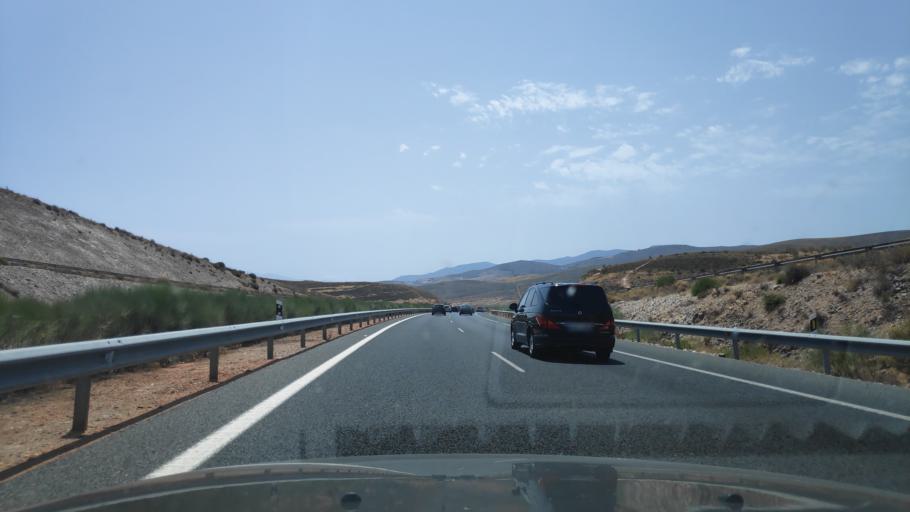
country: ES
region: Andalusia
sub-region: Provincia de Granada
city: Padul
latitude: 37.0002
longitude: -3.6310
